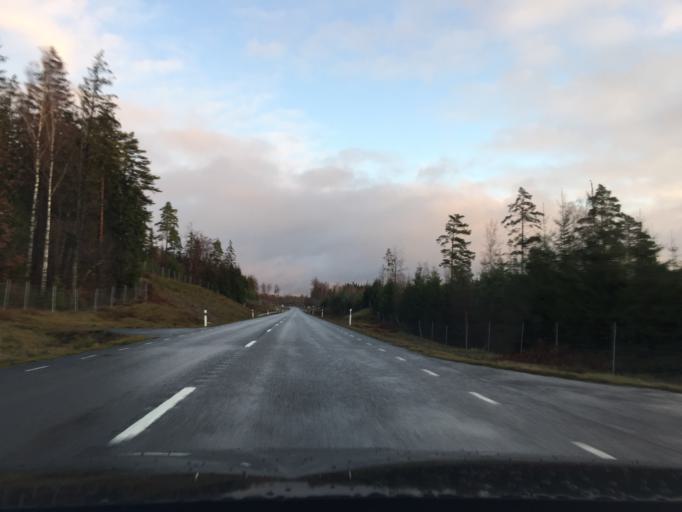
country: SE
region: Blekinge
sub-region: Karlshamns Kommun
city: Svangsta
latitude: 56.2895
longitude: 14.8747
